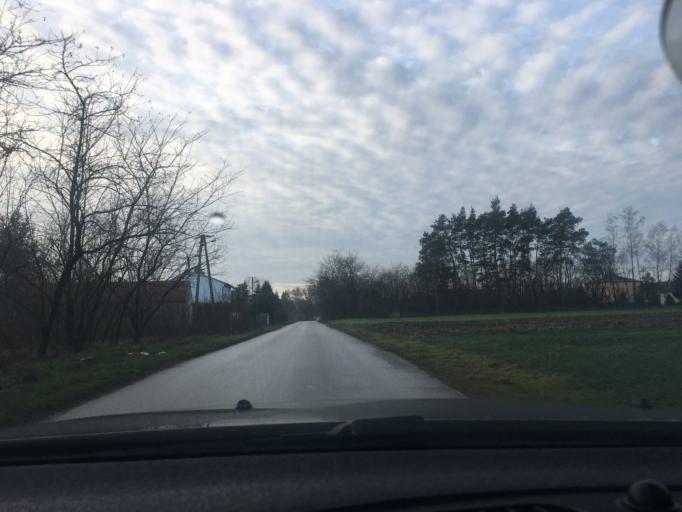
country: PL
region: Swietokrzyskie
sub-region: Powiat jedrzejowski
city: Imielno
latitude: 50.6333
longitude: 20.4096
